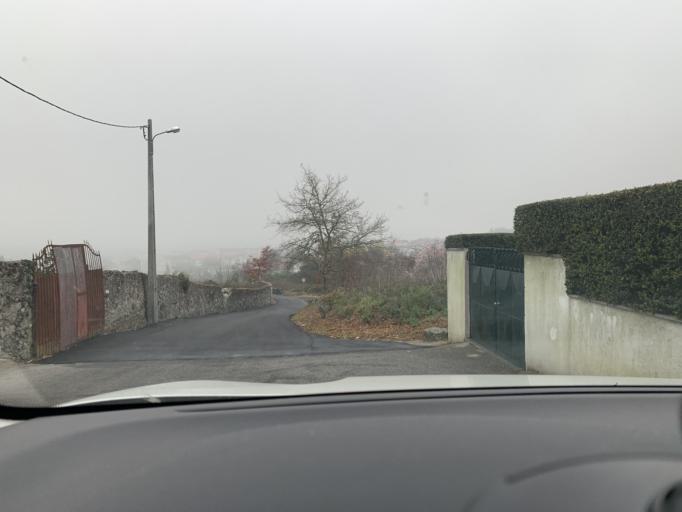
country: PT
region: Viseu
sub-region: Viseu
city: Viseu
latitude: 40.6580
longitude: -7.8962
